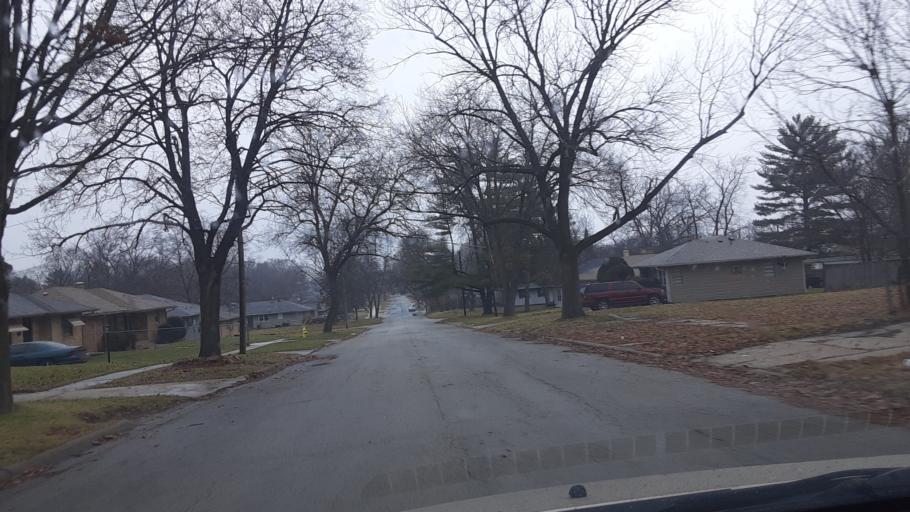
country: US
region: Illinois
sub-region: Winnebago County
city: Rockford
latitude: 42.2821
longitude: -89.1208
